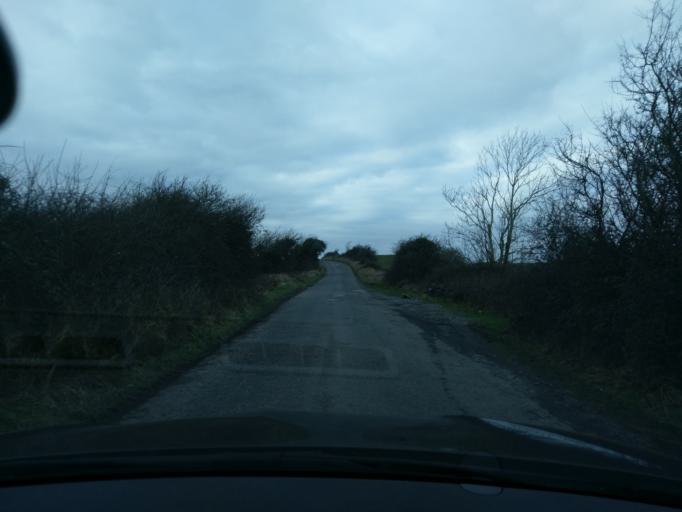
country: IE
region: Connaught
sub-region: County Galway
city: Gort
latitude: 53.1561
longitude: -8.8500
